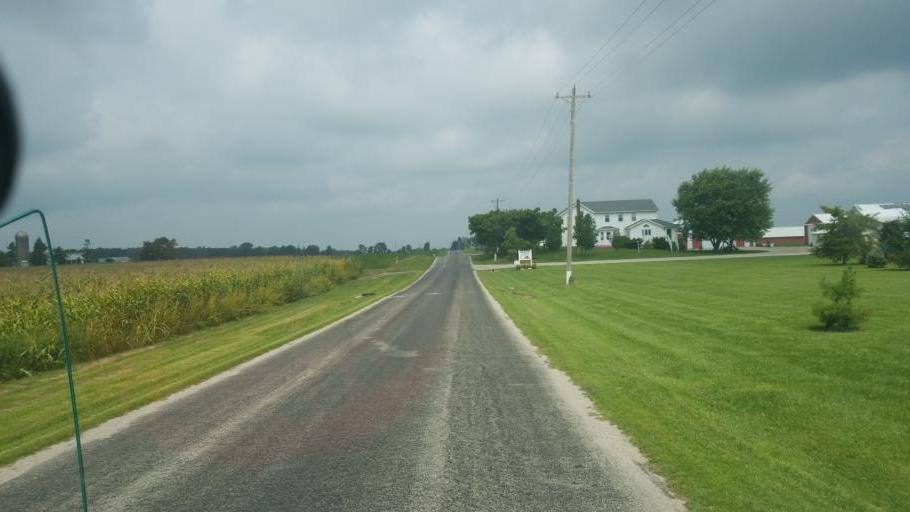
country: US
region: Ohio
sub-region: Huron County
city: Greenwich
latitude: 40.9955
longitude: -82.4810
